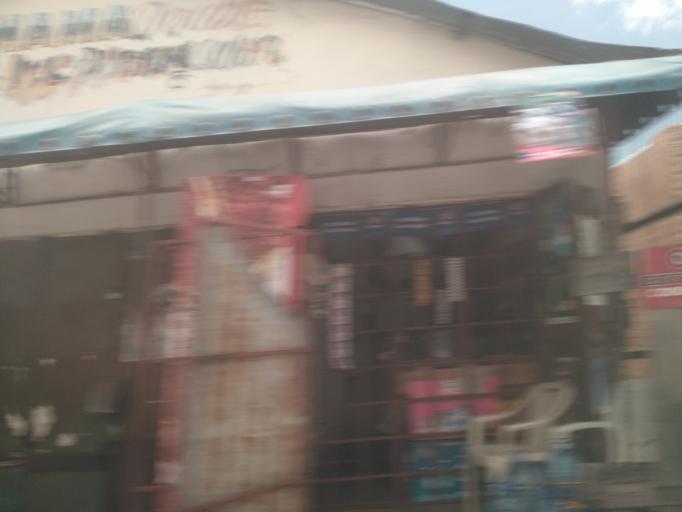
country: TZ
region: Dar es Salaam
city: Dar es Salaam
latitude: -6.8703
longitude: 39.2773
